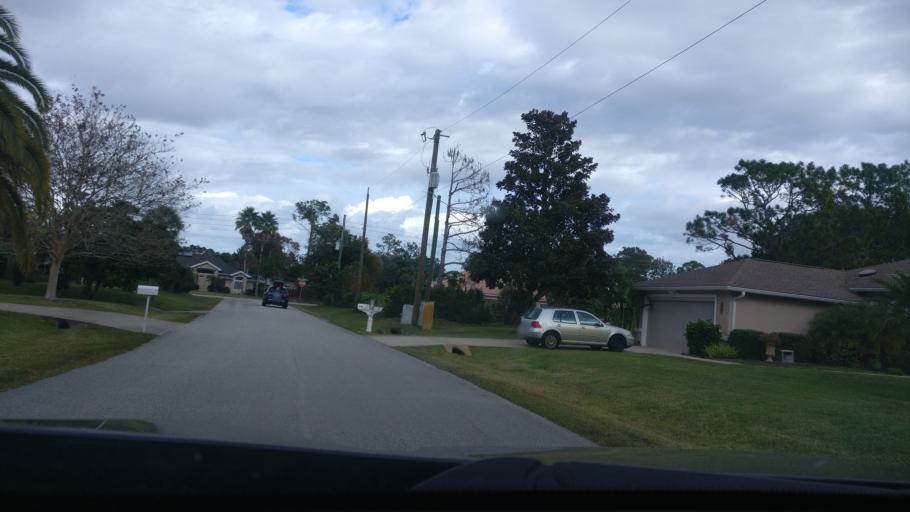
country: US
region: Florida
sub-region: Flagler County
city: Bunnell
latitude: 29.5226
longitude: -81.2337
